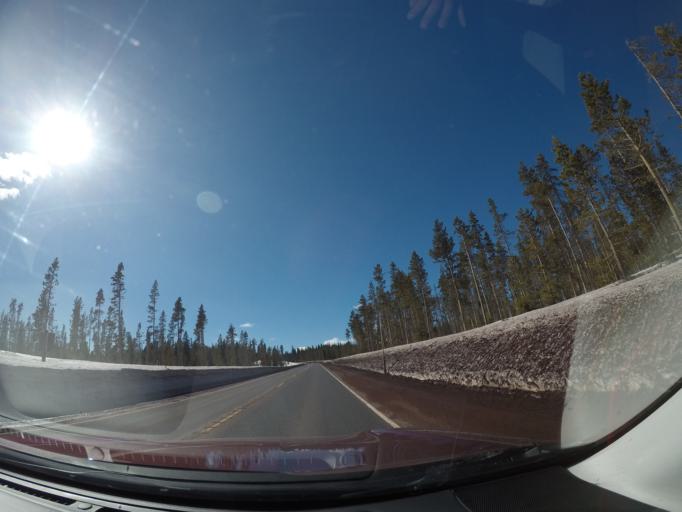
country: US
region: Oregon
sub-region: Deschutes County
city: Sunriver
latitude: 43.9867
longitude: -121.5734
